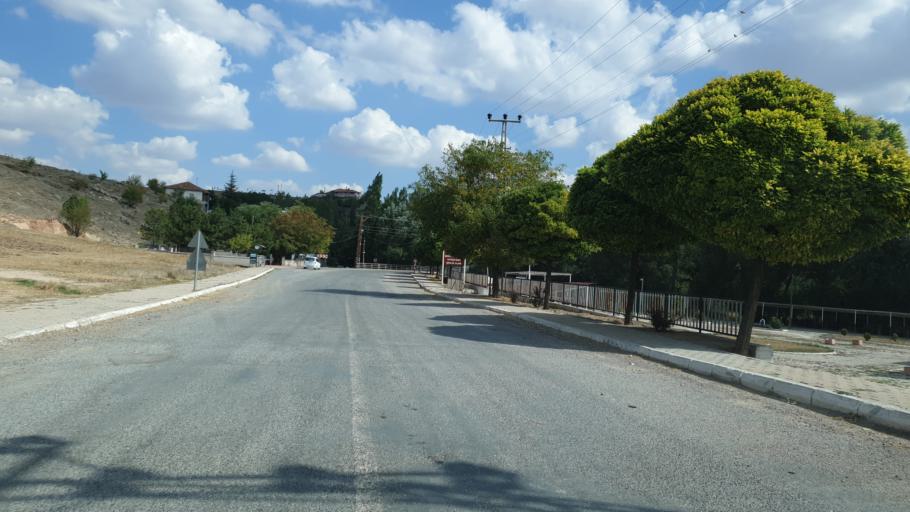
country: TR
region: Kayseri
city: Felahiye
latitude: 39.0947
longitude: 35.5620
